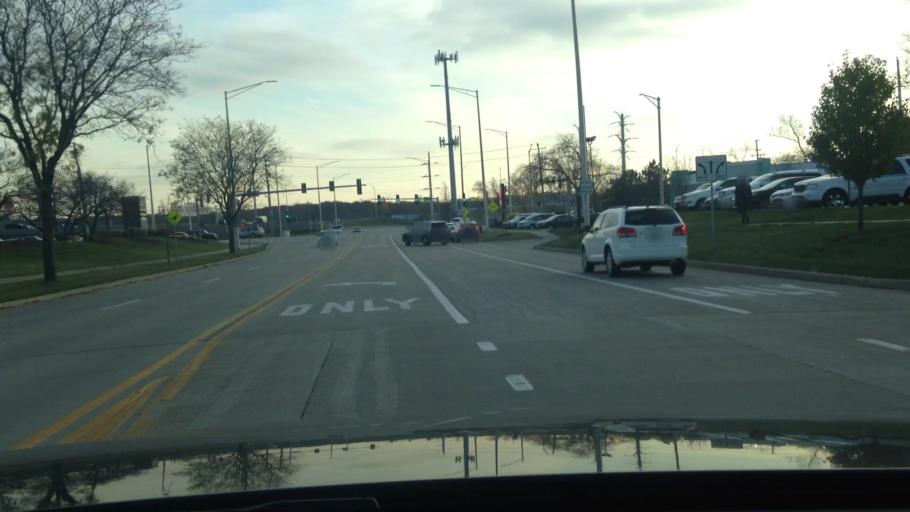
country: US
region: Illinois
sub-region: Cook County
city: Rolling Meadows
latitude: 42.0527
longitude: -88.0031
